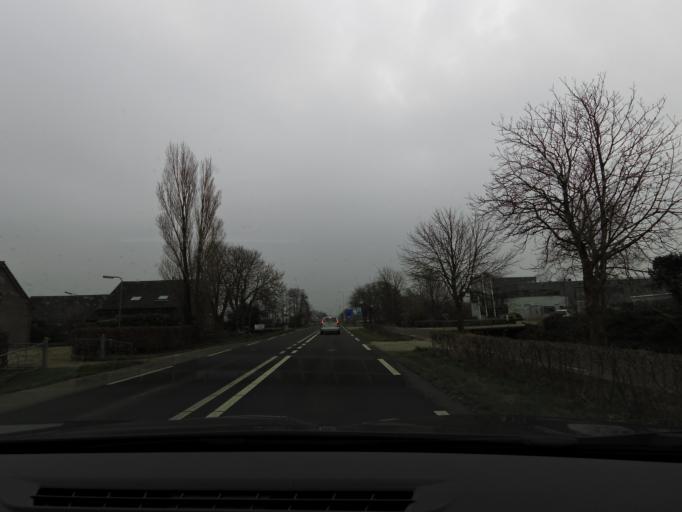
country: NL
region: South Holland
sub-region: Gemeente Nieuwkoop
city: Nieuwkoop
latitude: 52.1659
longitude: 4.7761
